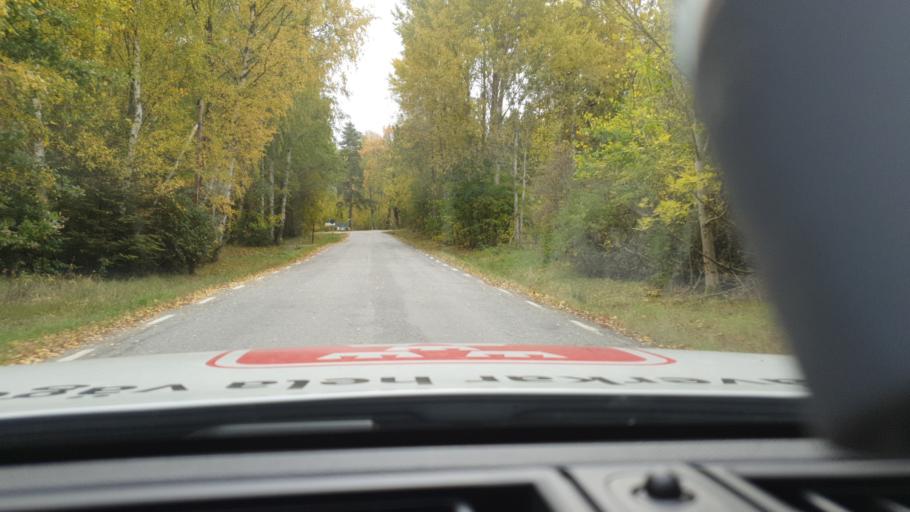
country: SE
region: Stockholm
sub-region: Upplands-Bro Kommun
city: Bro
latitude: 59.4896
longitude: 17.5671
